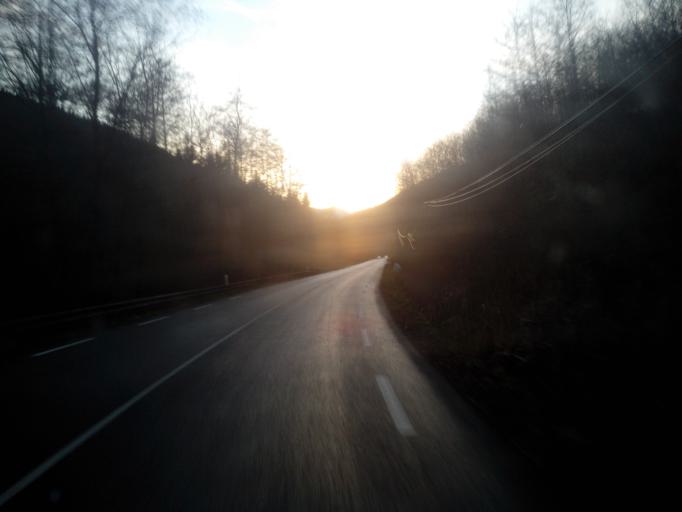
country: FR
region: Midi-Pyrenees
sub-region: Departement de l'Ariege
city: Saint-Paul-de-Jarrat
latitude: 42.9280
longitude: 1.7036
